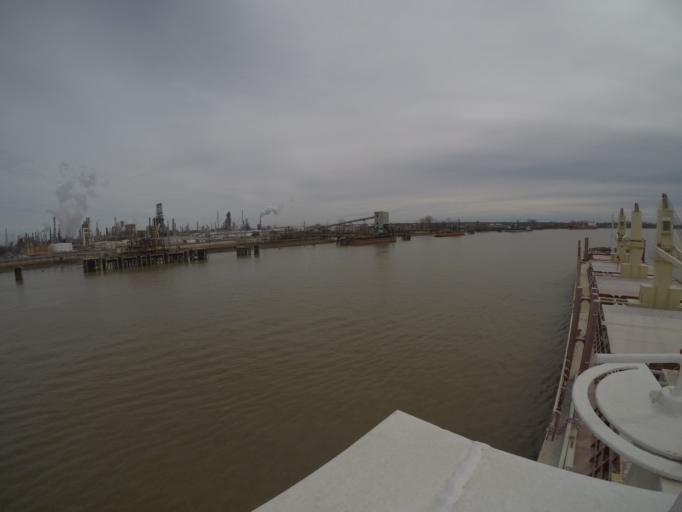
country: US
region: Louisiana
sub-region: Saint Charles Parish
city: Norco
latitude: 29.9898
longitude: -90.4064
